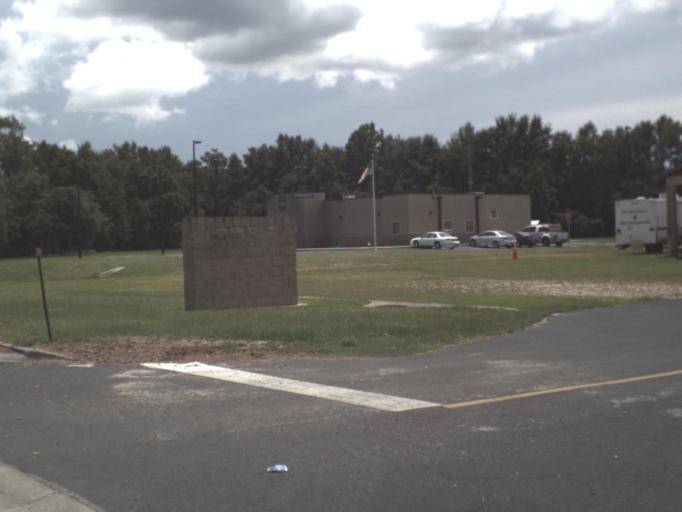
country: US
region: Florida
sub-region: Taylor County
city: Perry
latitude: 30.1107
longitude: -83.5728
